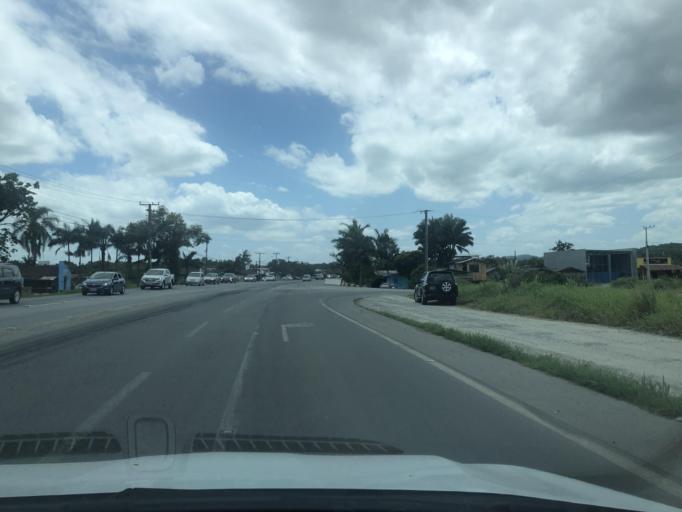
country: BR
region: Santa Catarina
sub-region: Joinville
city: Joinville
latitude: -26.4126
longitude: -48.7560
